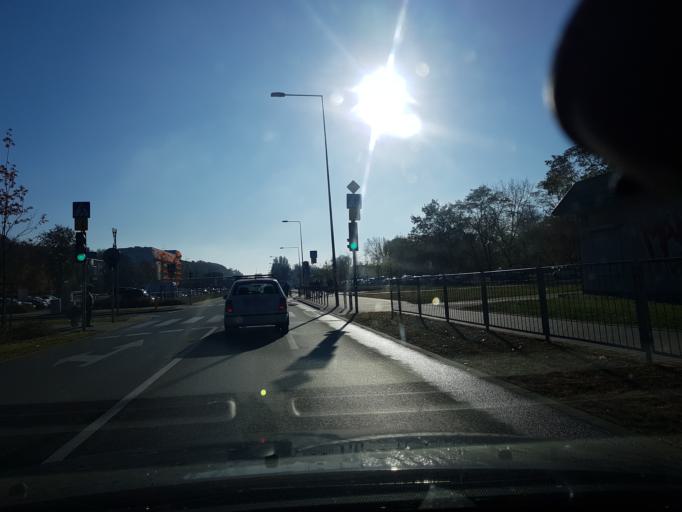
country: PL
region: Masovian Voivodeship
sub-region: Warszawa
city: Bielany
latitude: 52.2879
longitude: 20.9358
